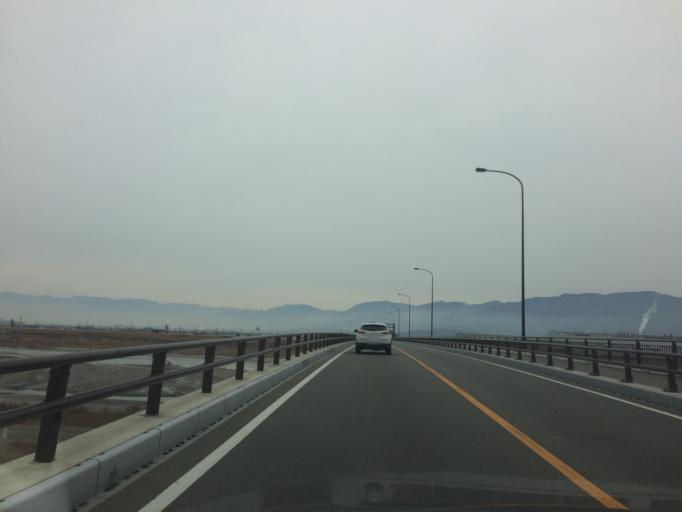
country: JP
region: Yamanashi
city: Ryuo
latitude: 35.5945
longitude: 138.5072
